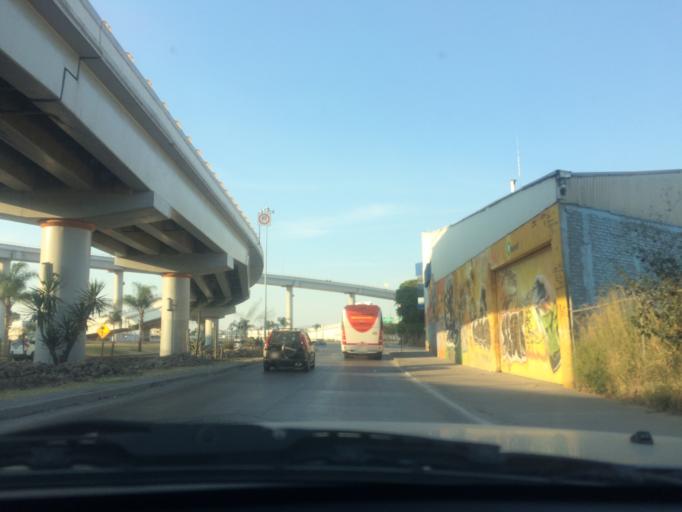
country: MX
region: Guanajuato
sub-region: Leon
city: Fraccionamiento Paraiso Real
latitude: 21.0952
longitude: -101.6261
